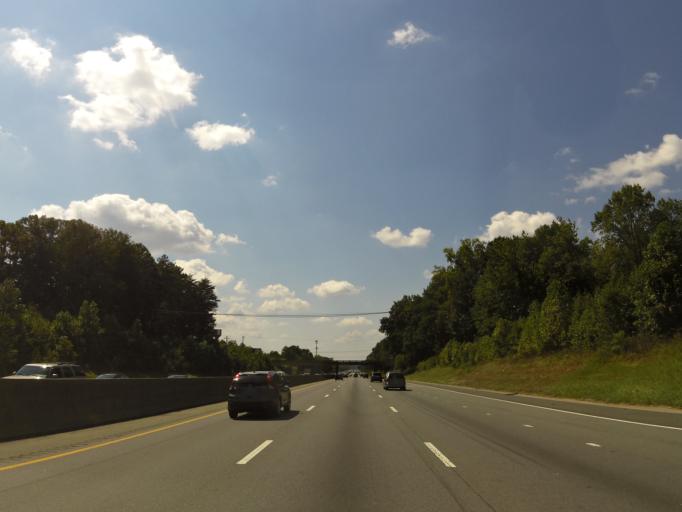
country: US
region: North Carolina
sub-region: Gaston County
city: Lowell
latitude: 35.2606
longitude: -81.1065
